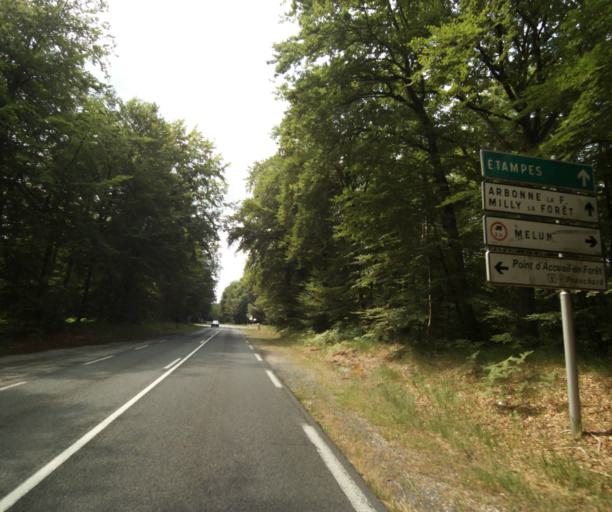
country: FR
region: Ile-de-France
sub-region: Departement de Seine-et-Marne
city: Barbizon
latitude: 48.4134
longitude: 2.6457
